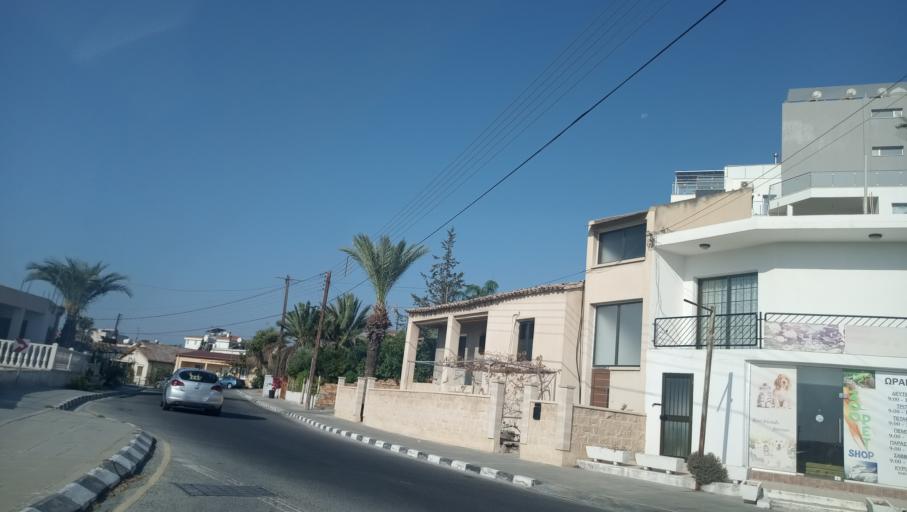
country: CY
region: Lefkosia
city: Geri
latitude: 35.1096
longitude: 33.4233
